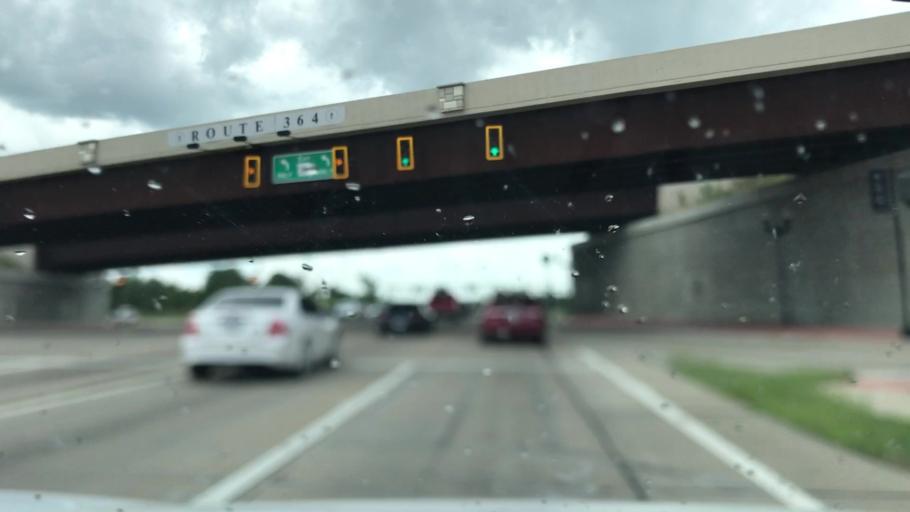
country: US
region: Missouri
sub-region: Saint Charles County
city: Dardenne Prairie
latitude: 38.7540
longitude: -90.7004
